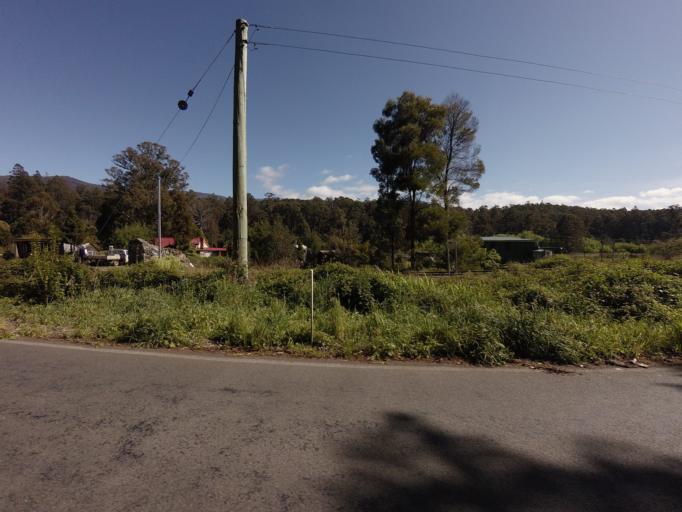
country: AU
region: Tasmania
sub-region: Derwent Valley
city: New Norfolk
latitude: -42.7128
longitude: 146.7013
